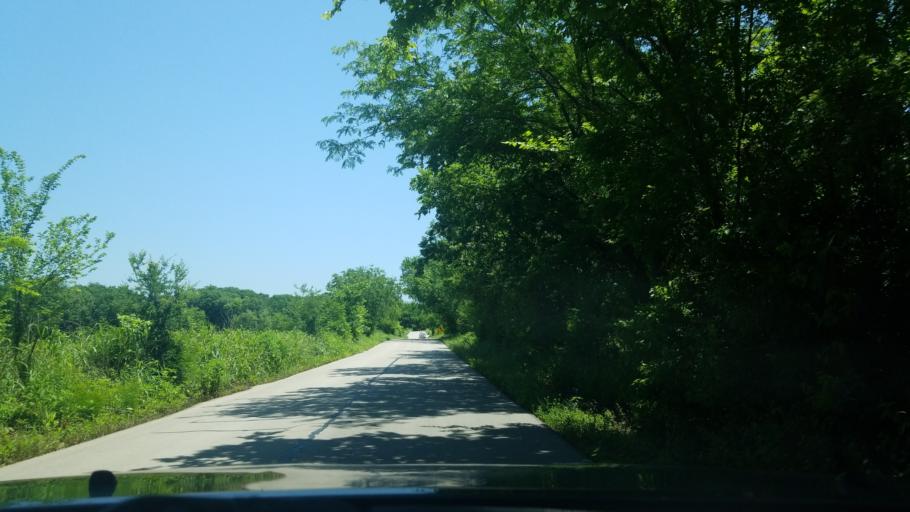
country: US
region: Texas
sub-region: Denton County
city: Sanger
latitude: 33.3468
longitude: -97.2201
